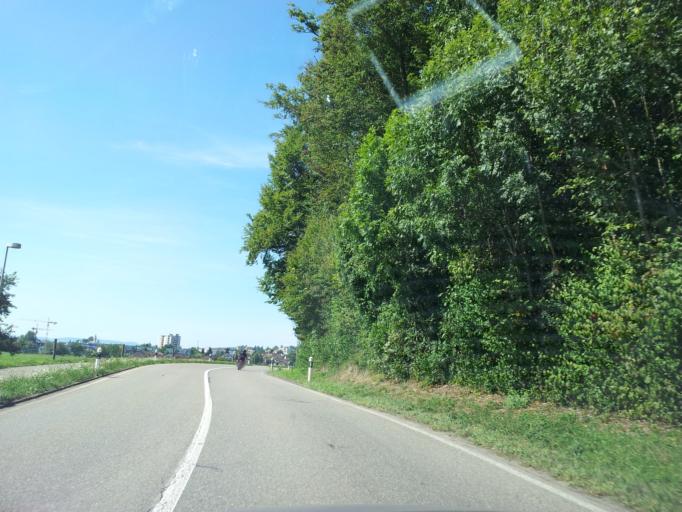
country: CH
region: Saint Gallen
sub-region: Wahlkreis See-Gaster
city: Jona
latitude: 47.2278
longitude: 8.8606
